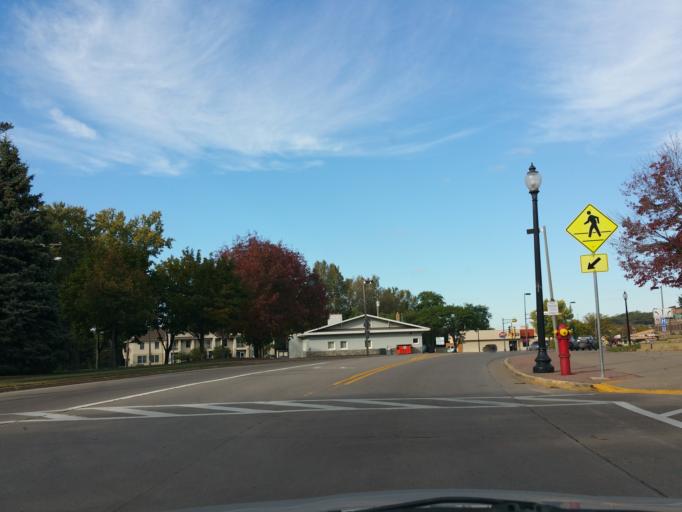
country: US
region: Wisconsin
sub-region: Pierce County
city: River Falls
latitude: 44.8530
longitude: -92.6293
